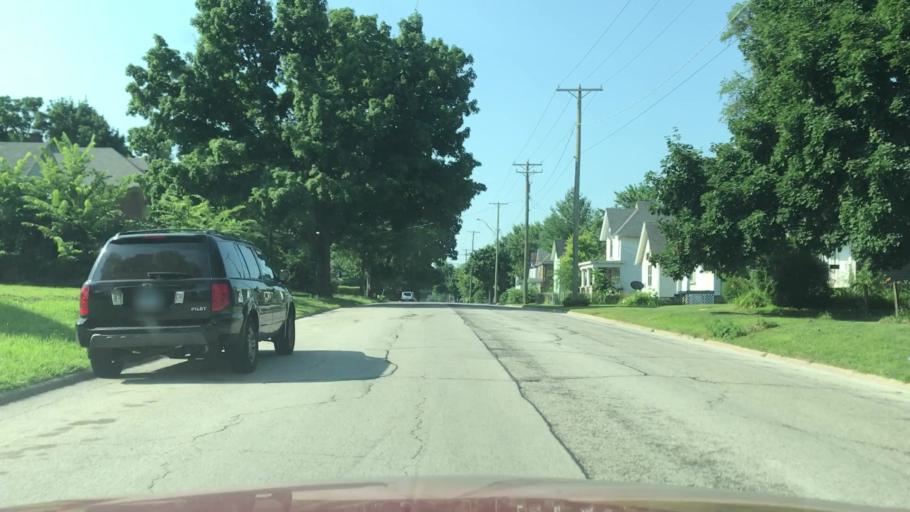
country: US
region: Illinois
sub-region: Winnebago County
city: Rockford
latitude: 42.2583
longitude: -89.0823
